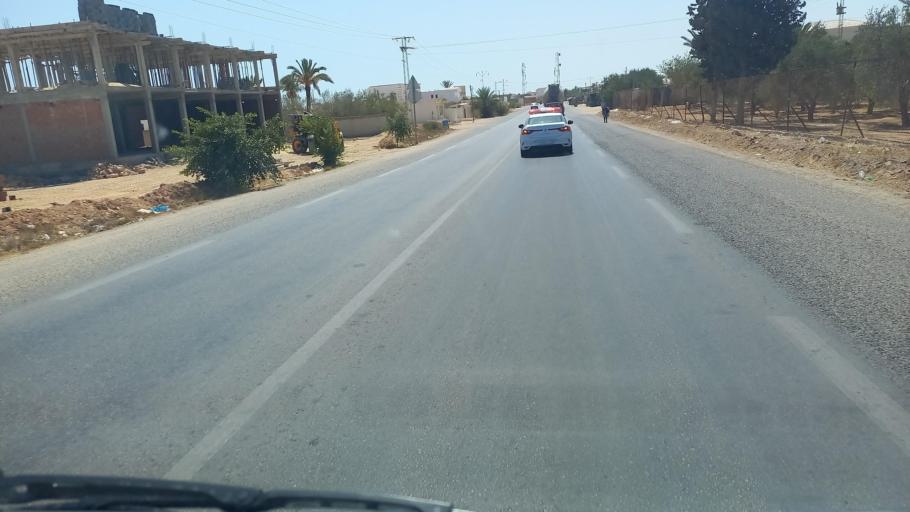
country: TN
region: Madanin
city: Houmt Souk
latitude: 33.8100
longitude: 10.8793
